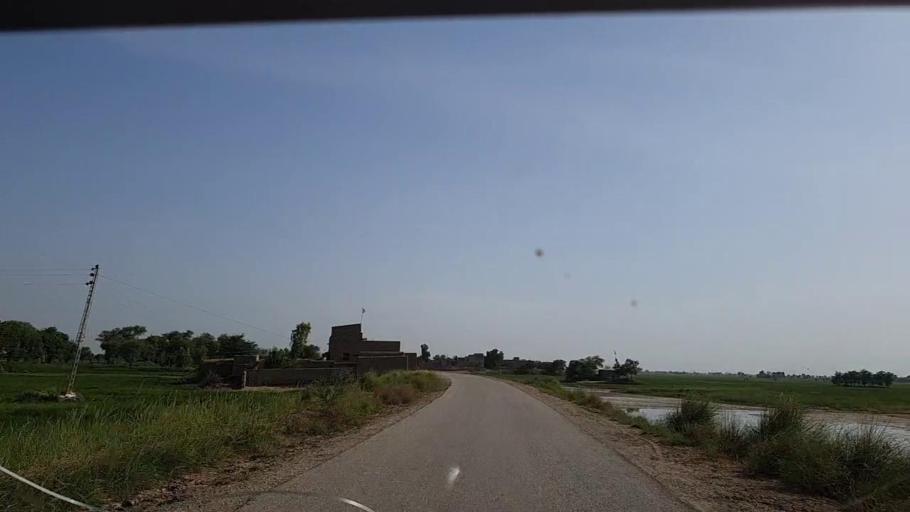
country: PK
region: Sindh
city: Khairpur Nathan Shah
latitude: 26.9996
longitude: 67.6670
